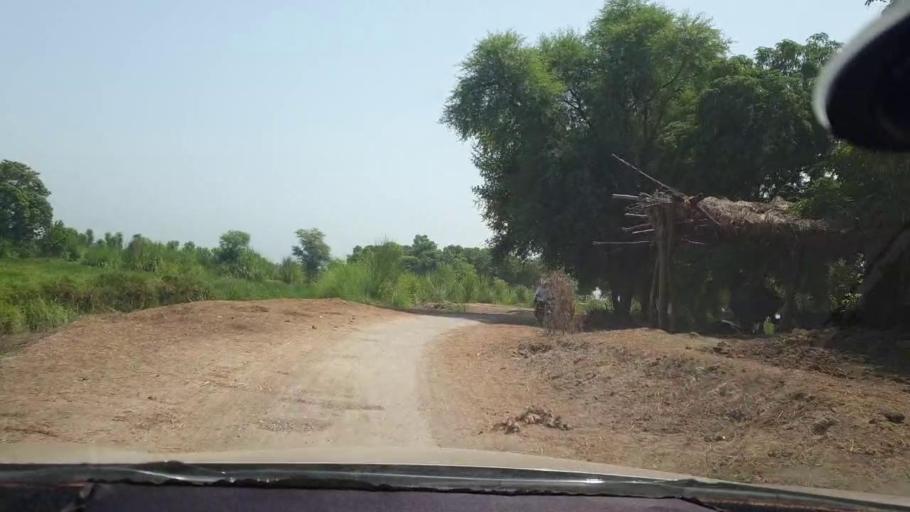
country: PK
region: Sindh
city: Kambar
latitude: 27.6653
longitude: 67.9445
